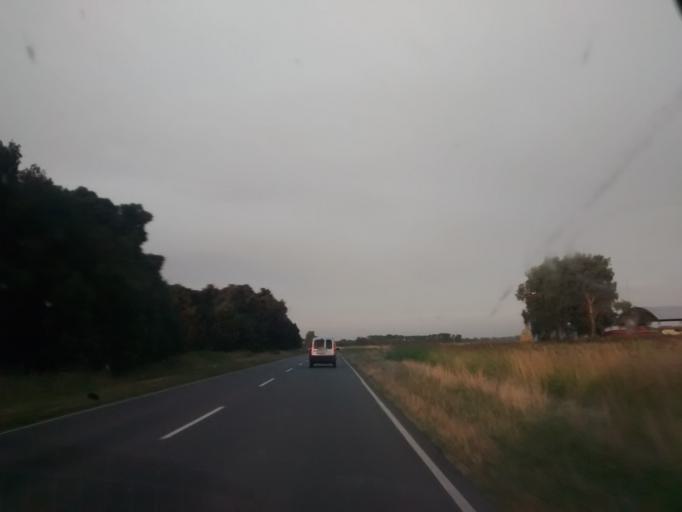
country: AR
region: Buenos Aires
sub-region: Partido de General Belgrano
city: General Belgrano
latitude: -35.8147
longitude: -58.5677
